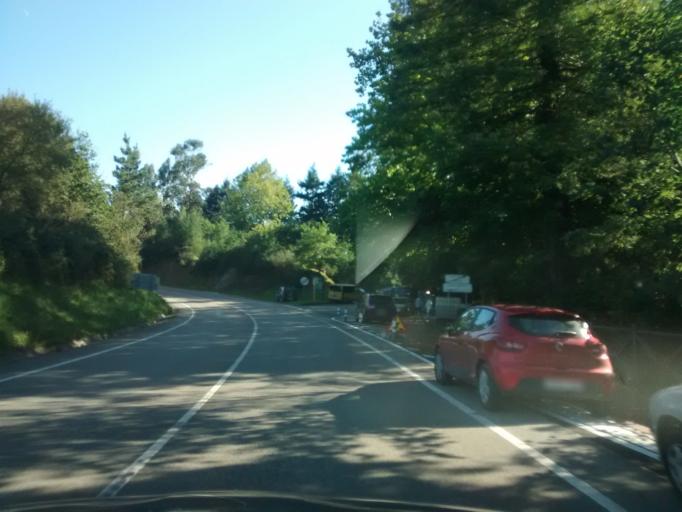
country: ES
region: Cantabria
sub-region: Provincia de Cantabria
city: Cabezon de la Sal
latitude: 43.3215
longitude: -4.2577
